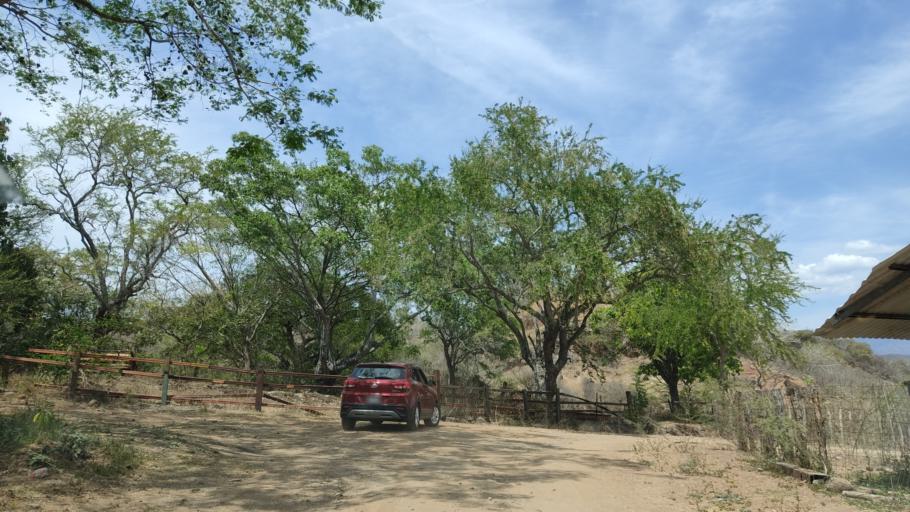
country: MX
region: Nayarit
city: Santa Maria del Oro
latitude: 21.5155
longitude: -104.5883
